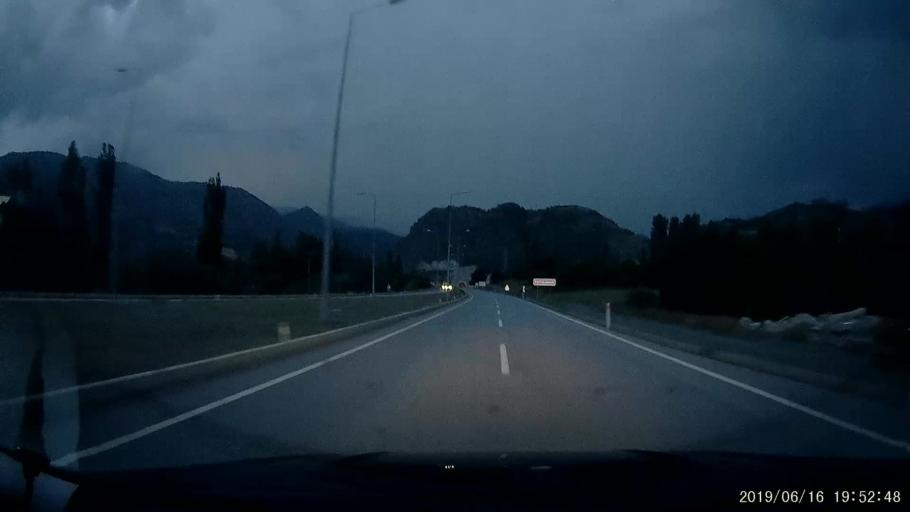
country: TR
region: Sivas
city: Koyulhisar
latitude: 40.2891
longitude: 37.7971
